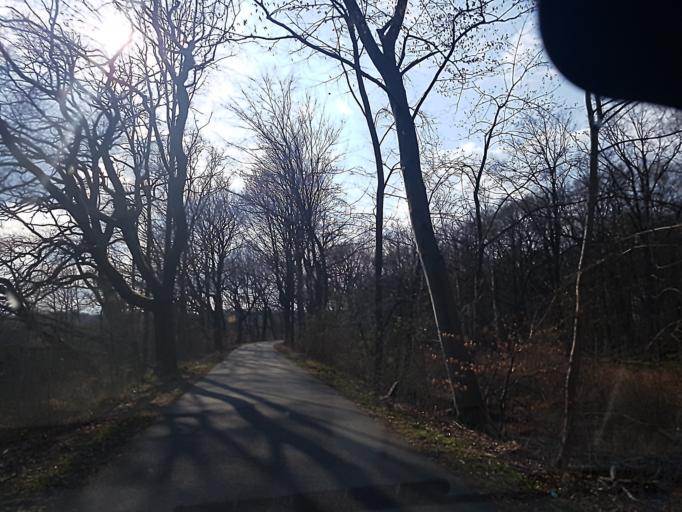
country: DE
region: Brandenburg
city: Doberlug-Kirchhain
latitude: 51.6105
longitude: 13.5335
